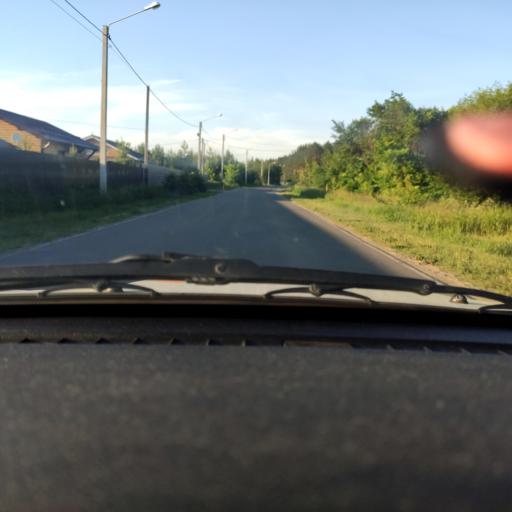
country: RU
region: Voronezj
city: Ramon'
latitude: 51.8905
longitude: 39.2717
